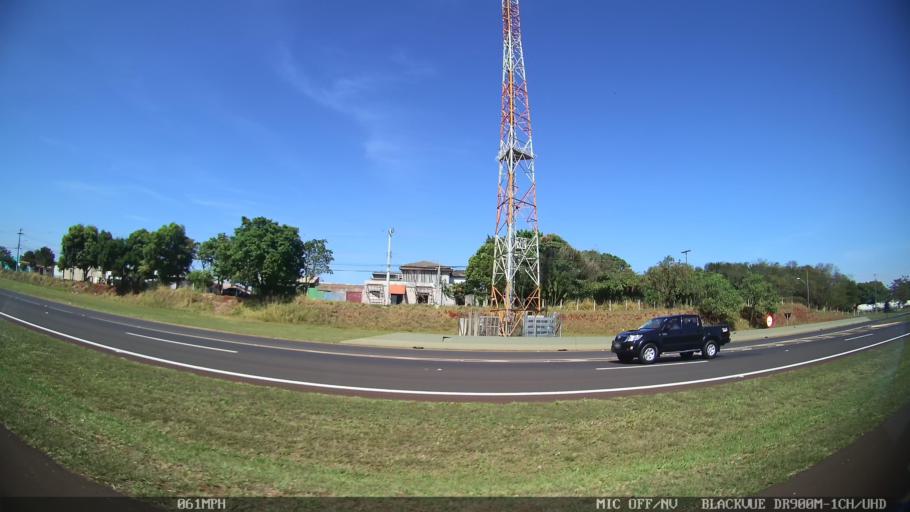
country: BR
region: Sao Paulo
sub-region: Ribeirao Preto
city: Ribeirao Preto
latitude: -21.1042
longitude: -47.8061
